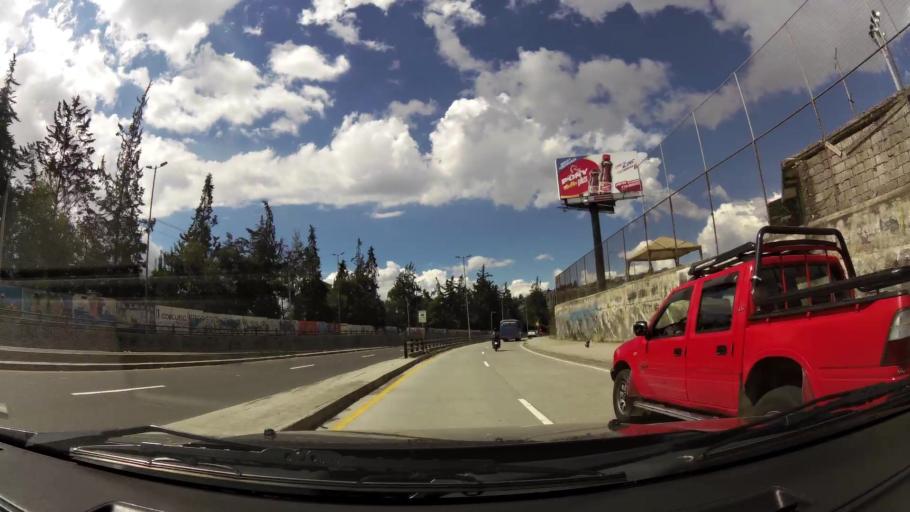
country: EC
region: Pichincha
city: Quito
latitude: -0.1030
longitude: -78.4939
